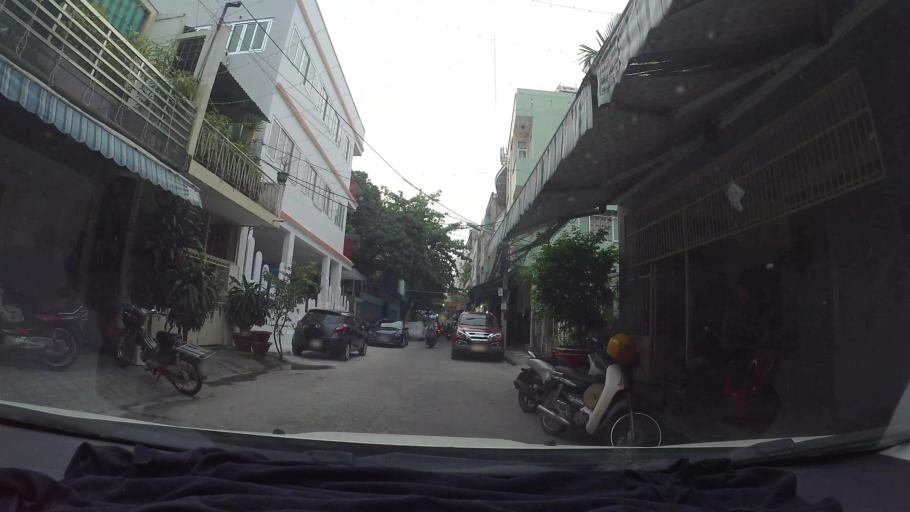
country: VN
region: Da Nang
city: Da Nang
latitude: 16.0740
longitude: 108.2216
